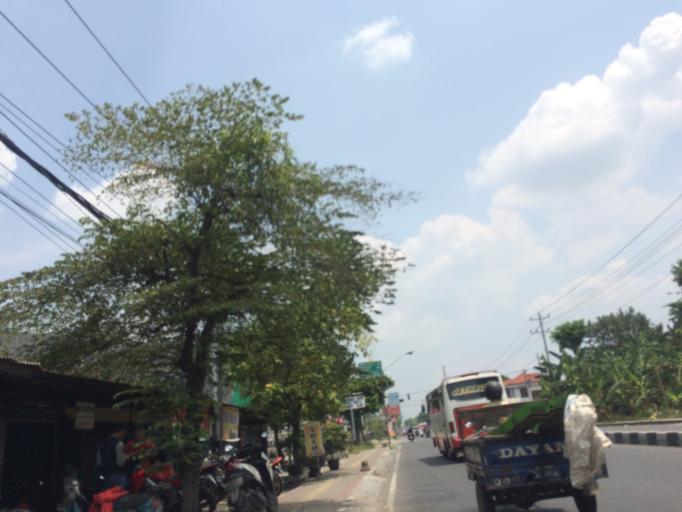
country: ID
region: Central Java
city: Grogol
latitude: -7.6209
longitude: 110.8213
